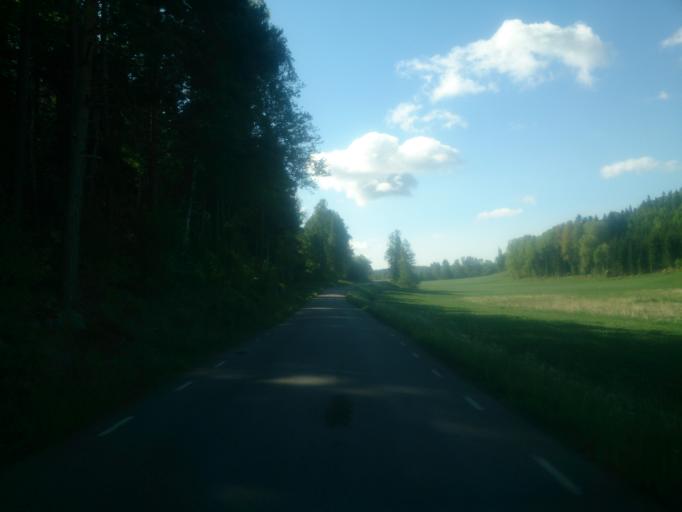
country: SE
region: OEstergoetland
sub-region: Atvidabergs Kommun
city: Atvidaberg
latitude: 58.3191
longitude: 16.0539
